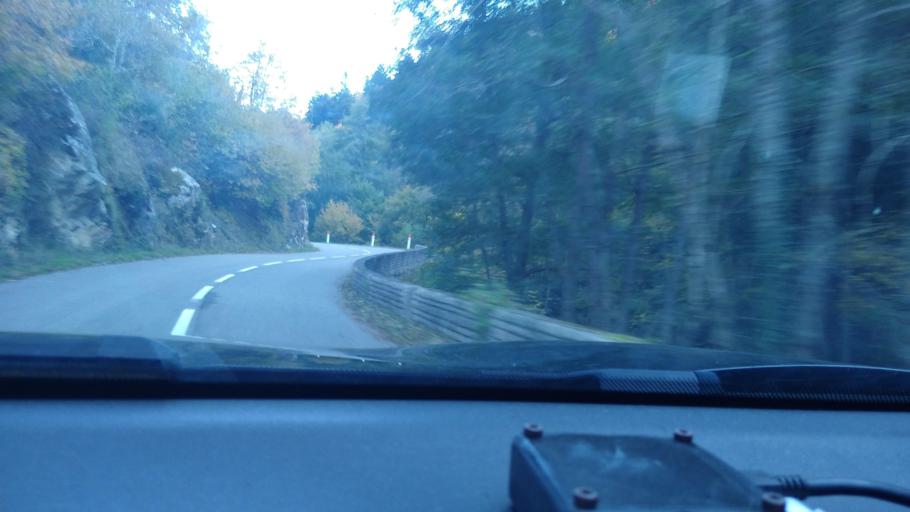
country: FR
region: Languedoc-Roussillon
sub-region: Departement de l'Aude
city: Quillan
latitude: 42.7324
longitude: 2.1003
